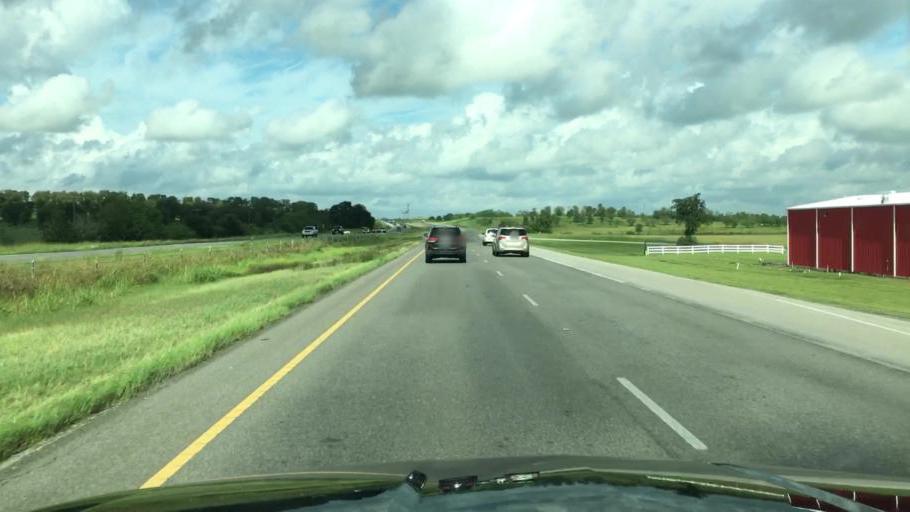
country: US
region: Texas
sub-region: Travis County
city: Garfield
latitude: 30.1665
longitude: -97.5114
